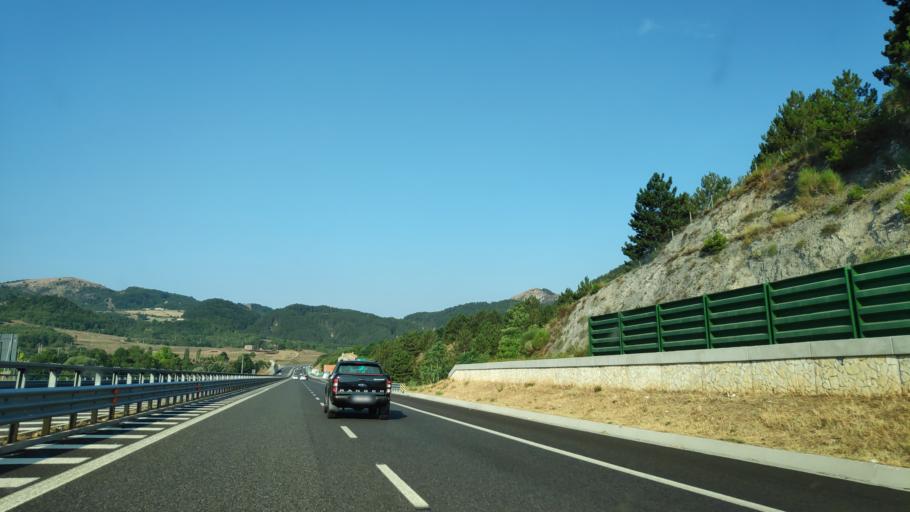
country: IT
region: Calabria
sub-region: Provincia di Cosenza
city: Mormanno
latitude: 39.8788
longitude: 16.0049
